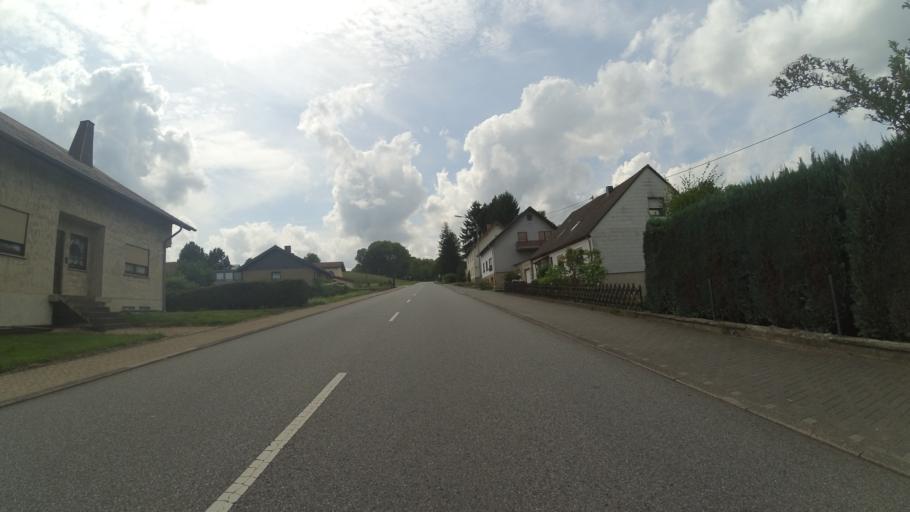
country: DE
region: Saarland
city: Tholey
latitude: 49.5352
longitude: 7.0316
